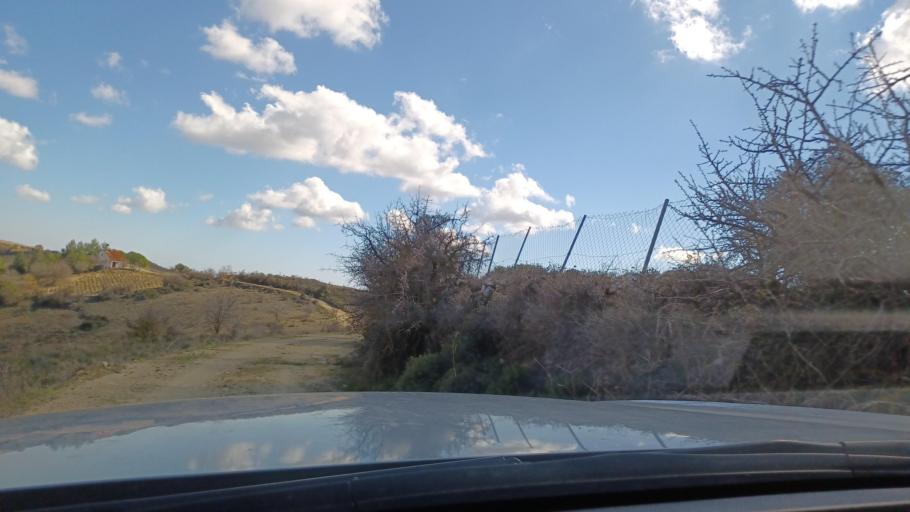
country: CY
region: Limassol
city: Pachna
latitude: 34.8248
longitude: 32.7634
